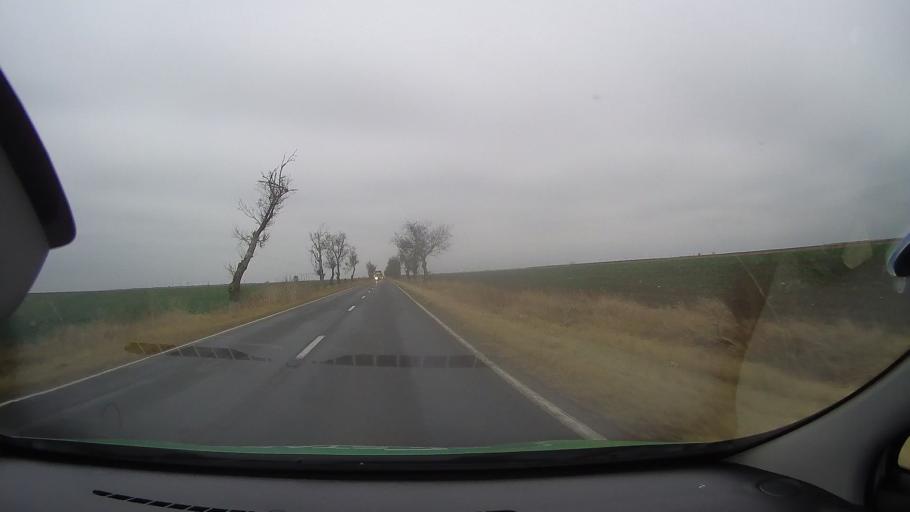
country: RO
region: Ialomita
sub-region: Comuna Scanteia
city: Scanteia
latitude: 44.7749
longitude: 27.4778
